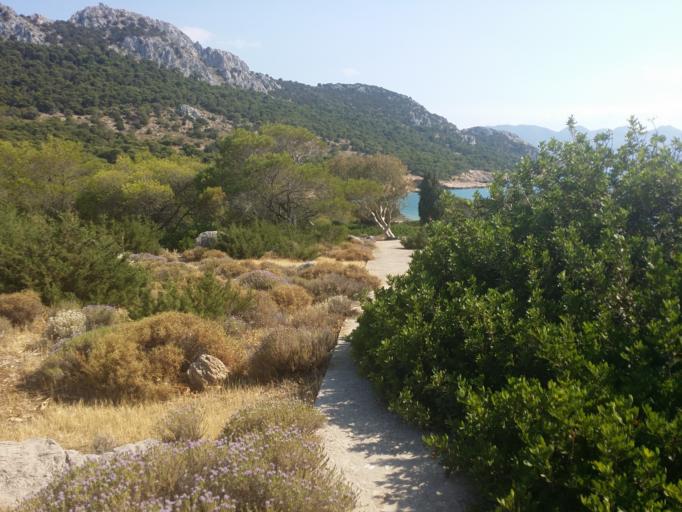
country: GR
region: Attica
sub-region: Nomos Piraios
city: Aegina
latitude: 37.6970
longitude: 23.4335
